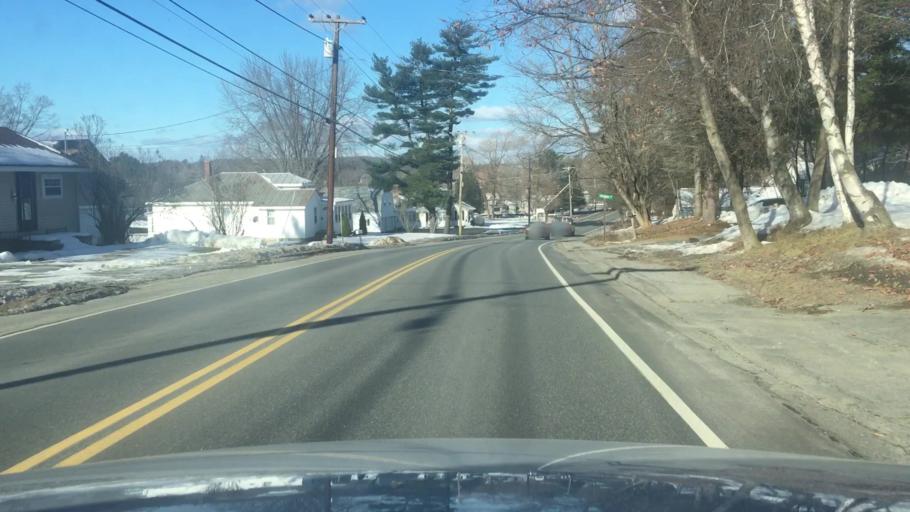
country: US
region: Maine
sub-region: Somerset County
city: Skowhegan
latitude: 44.7542
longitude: -69.7099
